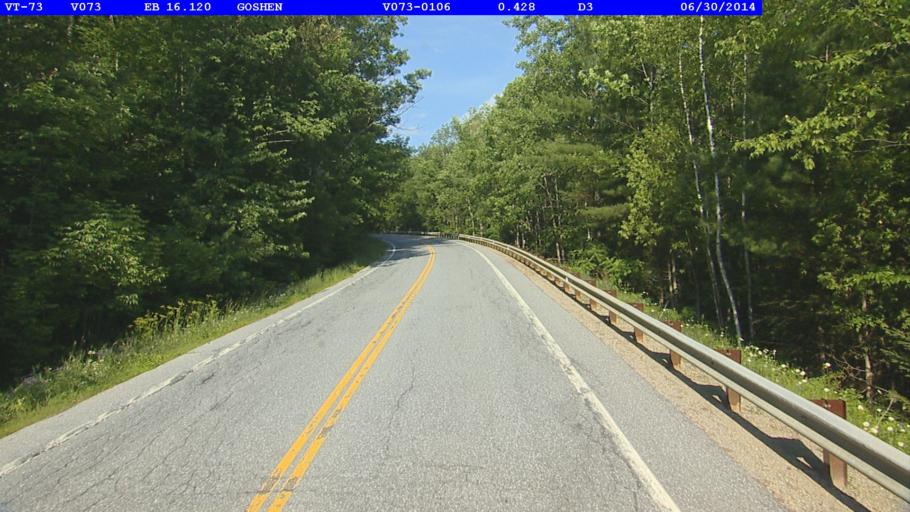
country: US
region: Vermont
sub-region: Rutland County
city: Brandon
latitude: 43.8423
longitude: -73.0215
